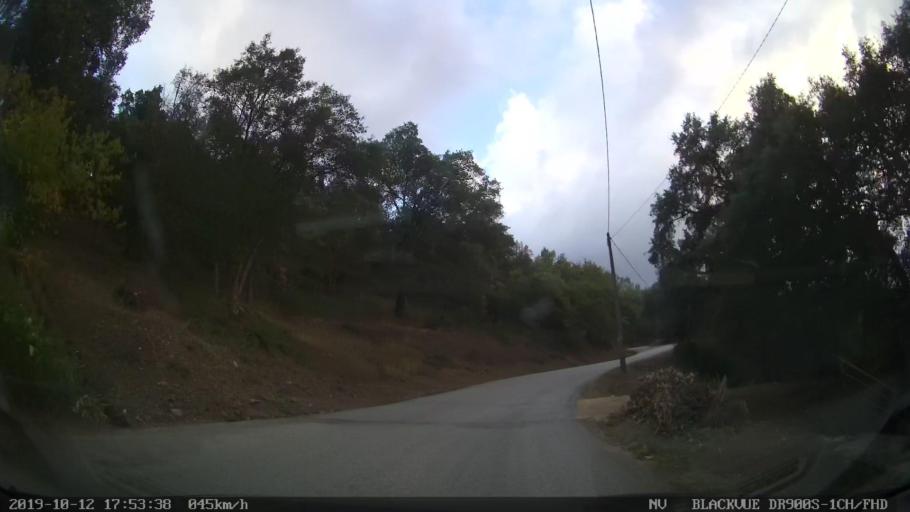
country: PT
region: Vila Real
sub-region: Mesao Frio
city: Mesao Frio
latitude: 41.1642
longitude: -7.8596
